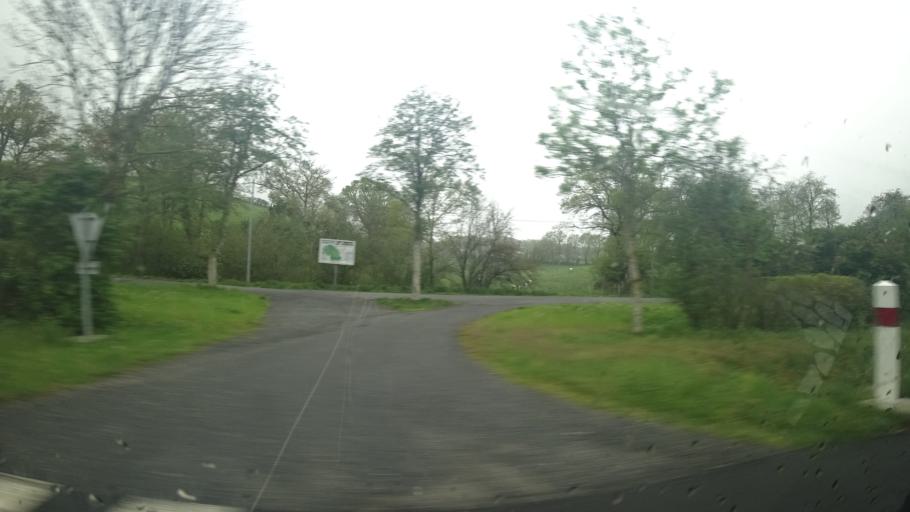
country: FR
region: Midi-Pyrenees
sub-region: Departement de l'Aveyron
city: Laissac
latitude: 44.2771
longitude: 2.8627
